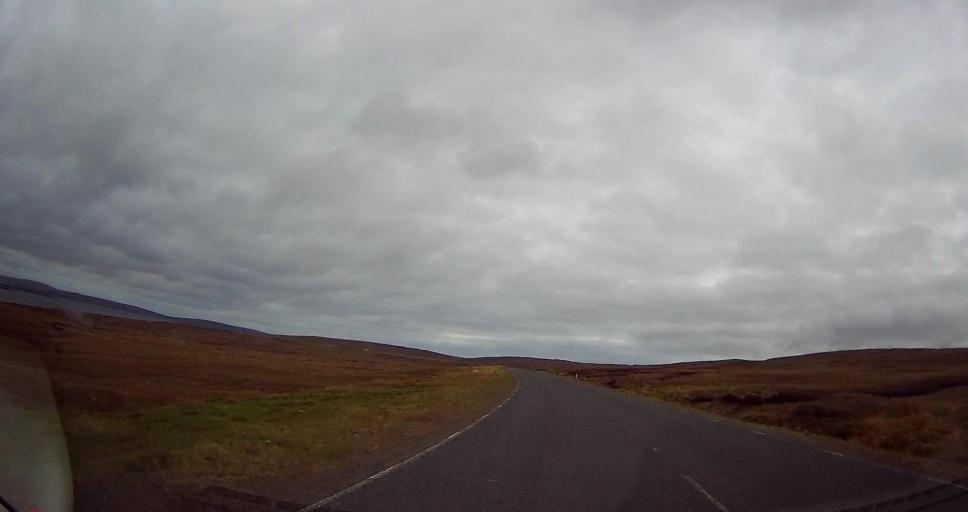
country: GB
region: Scotland
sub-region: Shetland Islands
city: Shetland
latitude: 60.6435
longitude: -1.0720
